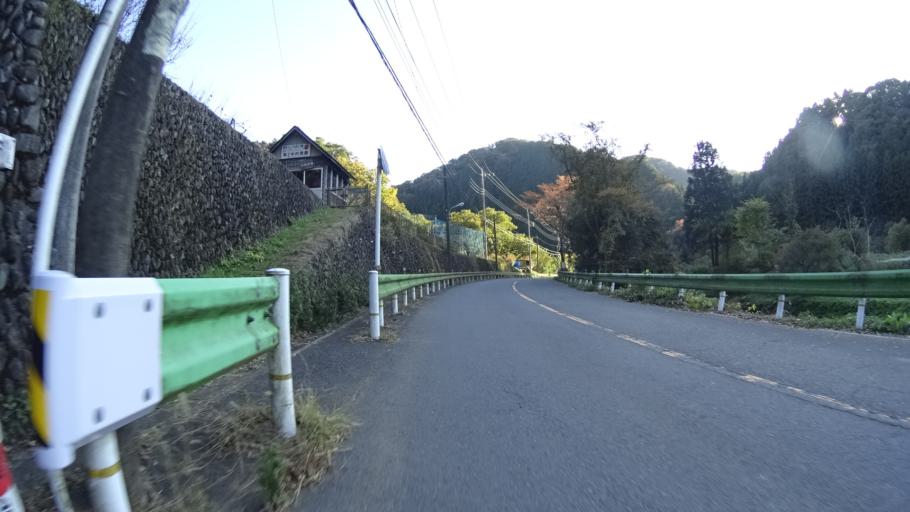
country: JP
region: Tokyo
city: Itsukaichi
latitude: 35.6740
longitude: 139.2237
